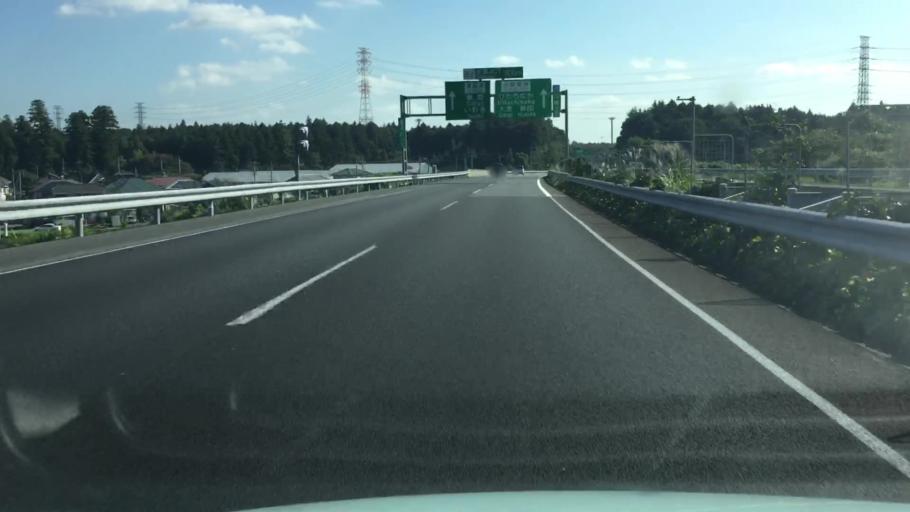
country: JP
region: Ibaraki
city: Tomobe
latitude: 36.3195
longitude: 140.3383
